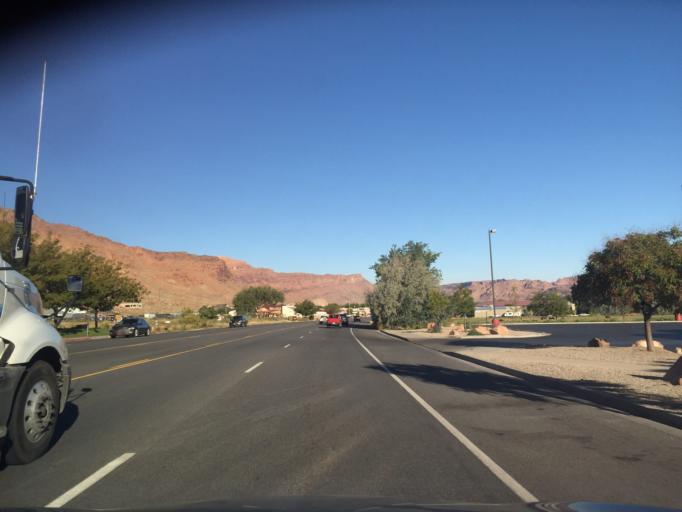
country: US
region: Utah
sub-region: Grand County
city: Moab
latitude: 38.5580
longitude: -109.5436
